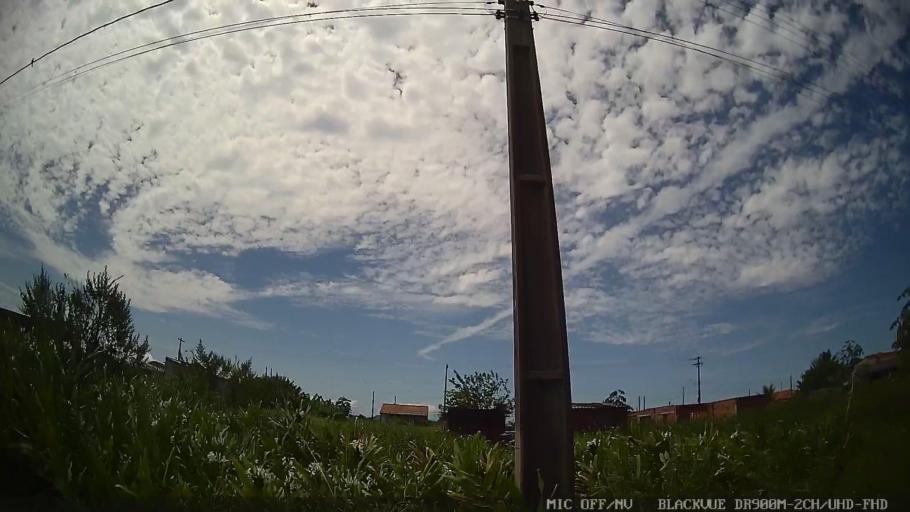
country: BR
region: Sao Paulo
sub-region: Iguape
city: Iguape
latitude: -24.7263
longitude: -47.5192
